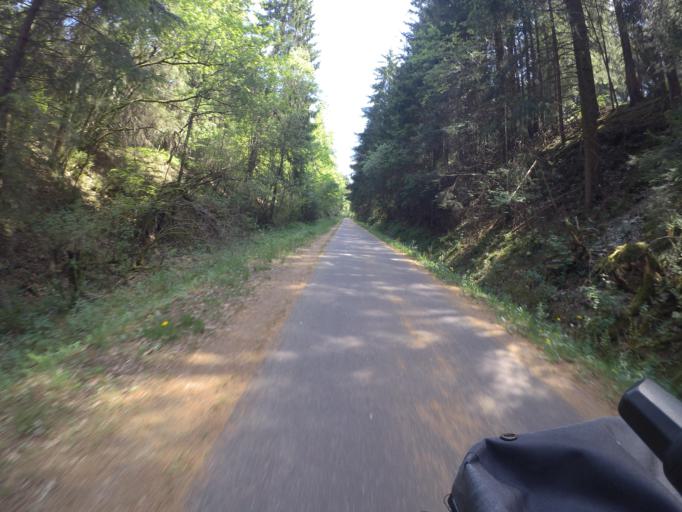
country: BE
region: Wallonia
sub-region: Province de Liege
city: Butgenbach
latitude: 50.4236
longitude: 6.2311
